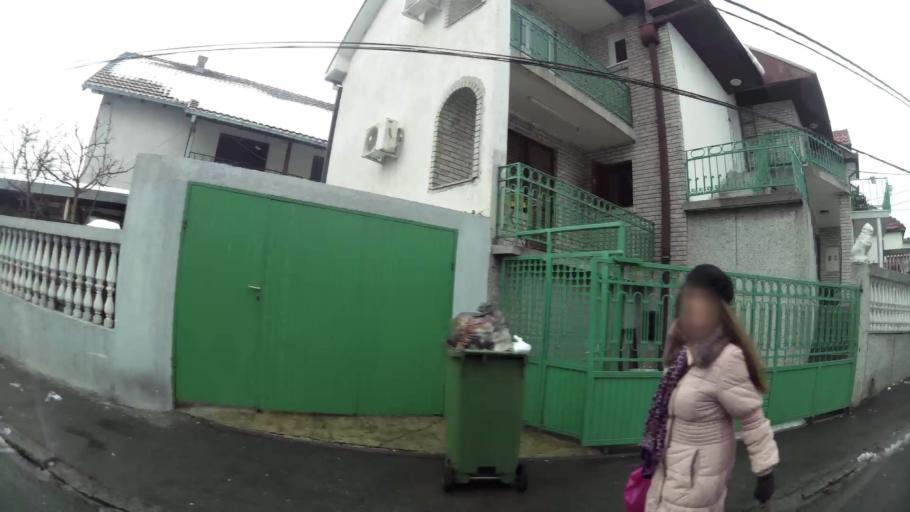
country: RS
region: Central Serbia
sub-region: Belgrade
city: Zvezdara
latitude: 44.7770
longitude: 20.5234
